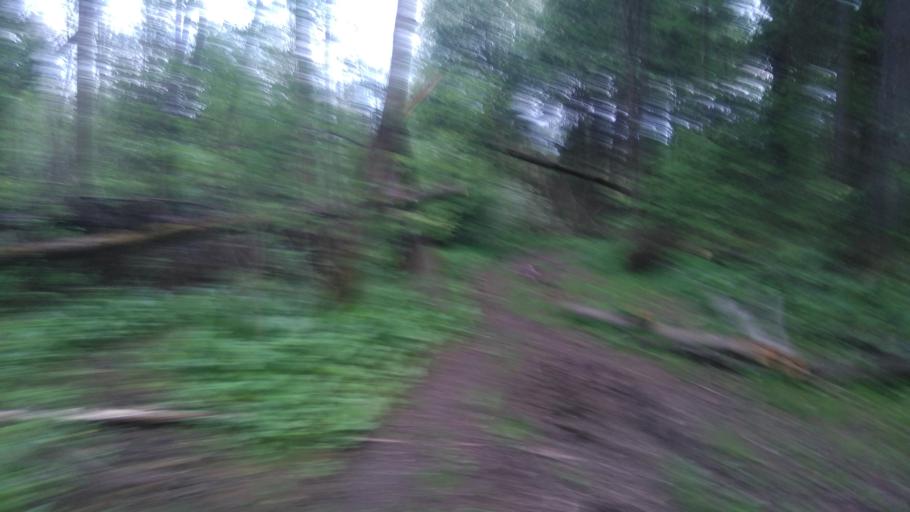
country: RU
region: Perm
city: Froly
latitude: 57.9655
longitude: 56.2986
